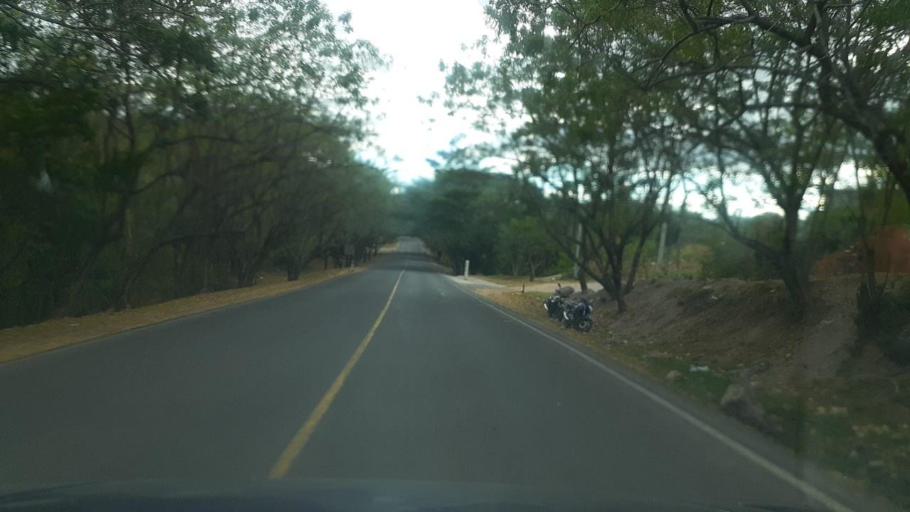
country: NI
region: Madriz
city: Somoto
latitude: 13.5003
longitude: -86.5722
